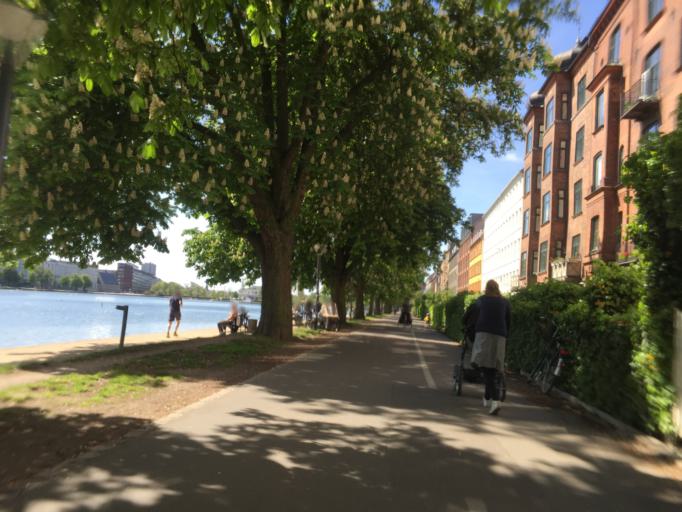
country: DK
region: Capital Region
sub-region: Kobenhavn
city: Copenhagen
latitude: 55.6859
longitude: 12.5610
